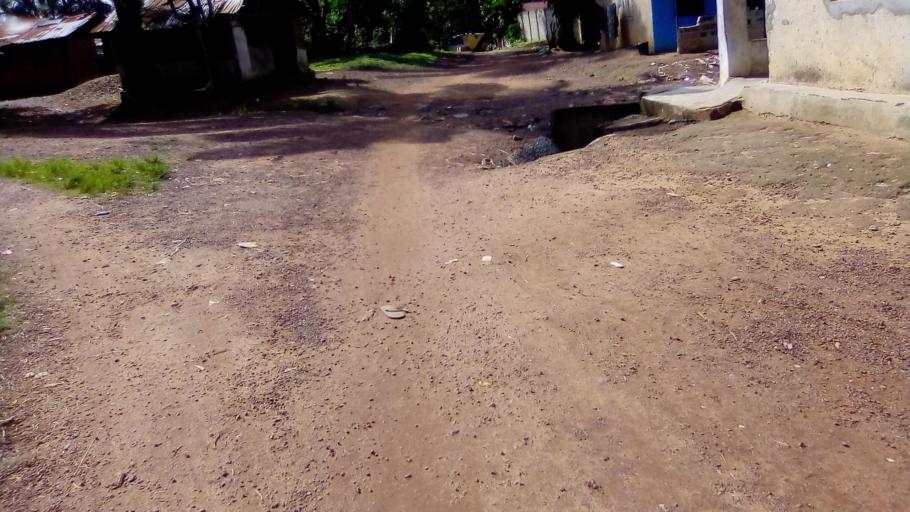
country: SL
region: Southern Province
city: Bo
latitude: 7.9766
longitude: -11.7272
